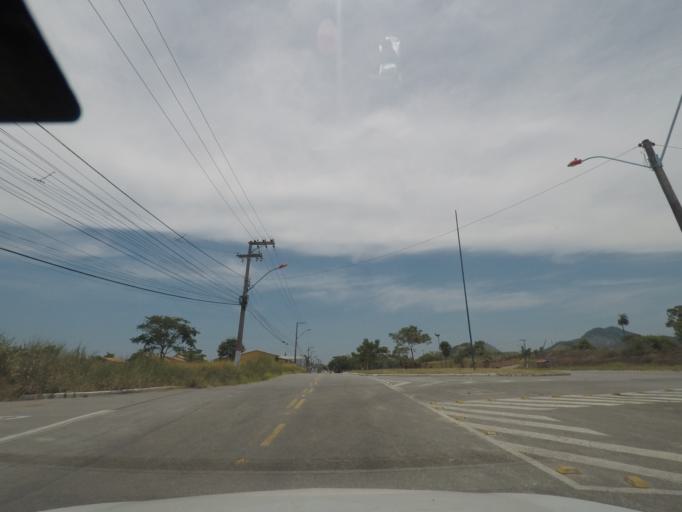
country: BR
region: Rio de Janeiro
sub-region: Marica
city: Marica
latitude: -22.9141
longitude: -42.8458
